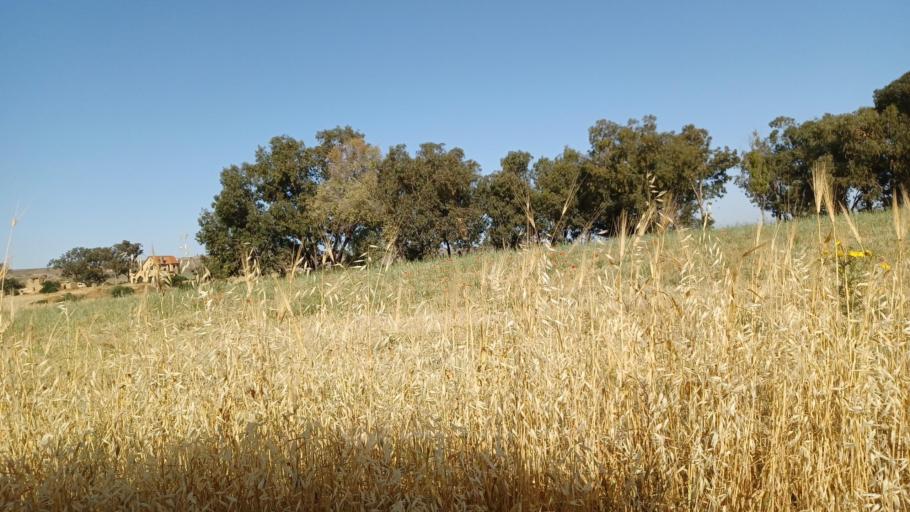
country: CY
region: Lefkosia
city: Mammari
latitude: 35.1689
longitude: 33.2488
